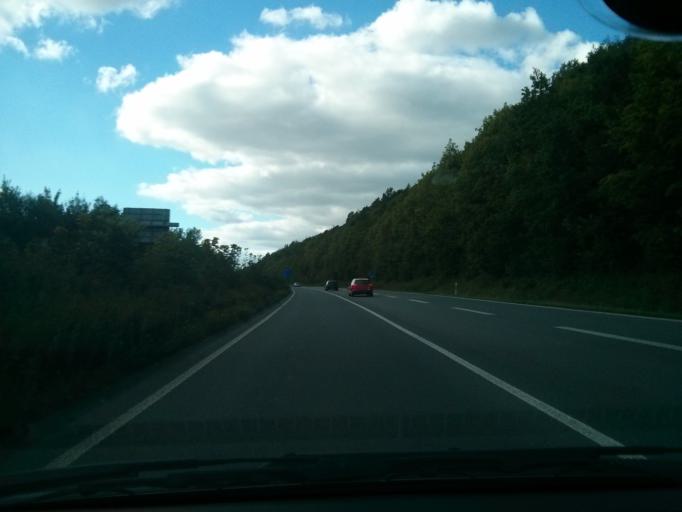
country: DE
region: North Rhine-Westphalia
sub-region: Regierungsbezirk Arnsberg
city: Arnsberg
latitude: 51.4399
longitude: 7.9879
